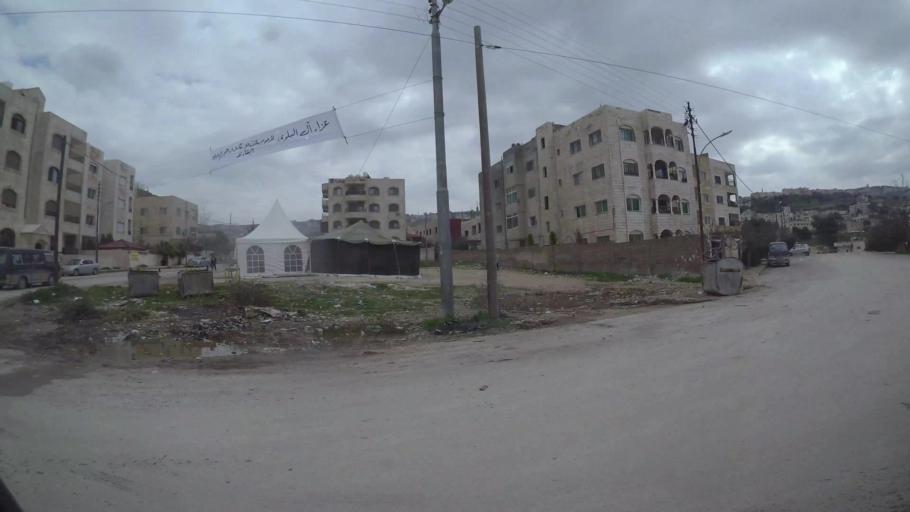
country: JO
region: Amman
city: Al Jubayhah
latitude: 32.0550
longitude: 35.8398
